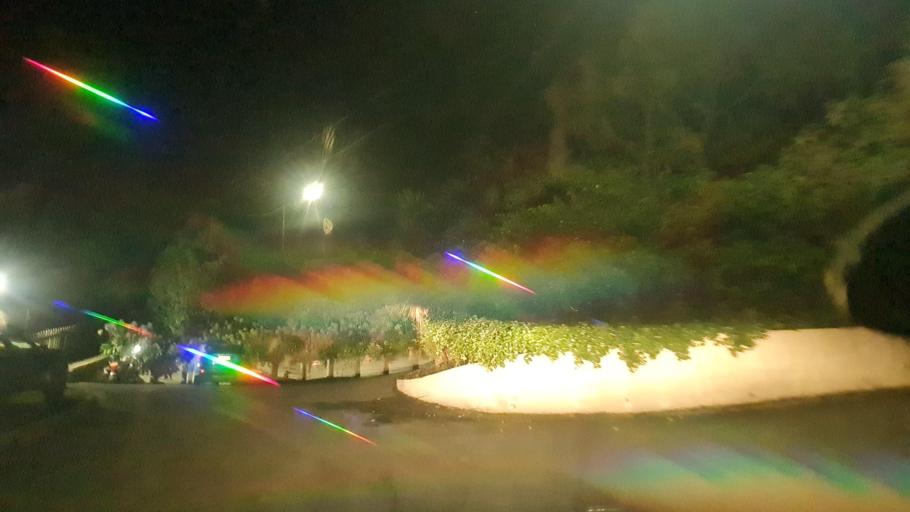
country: NZ
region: Otago
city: Oamaru
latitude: -45.0895
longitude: 170.9710
